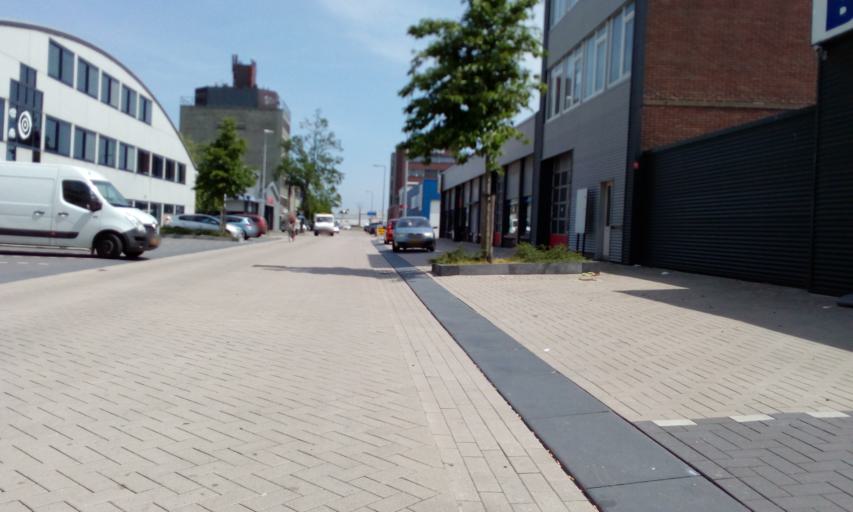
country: NL
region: South Holland
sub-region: Gemeente Schiedam
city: Schiedam
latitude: 51.9248
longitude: 4.4127
